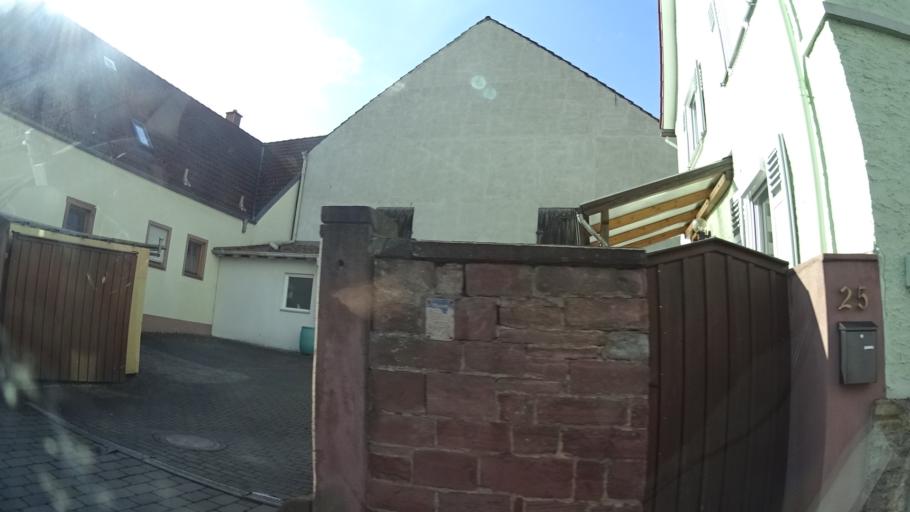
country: DE
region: Baden-Wuerttemberg
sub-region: Regierungsbezirk Stuttgart
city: Werbach
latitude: 49.6798
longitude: 9.6796
